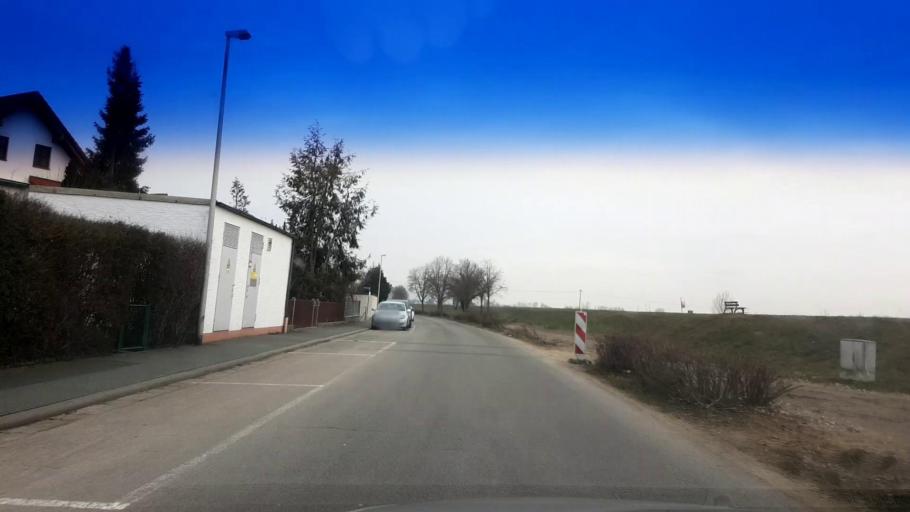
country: DE
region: Bavaria
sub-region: Upper Franconia
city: Hirschaid
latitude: 49.8132
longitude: 10.9881
